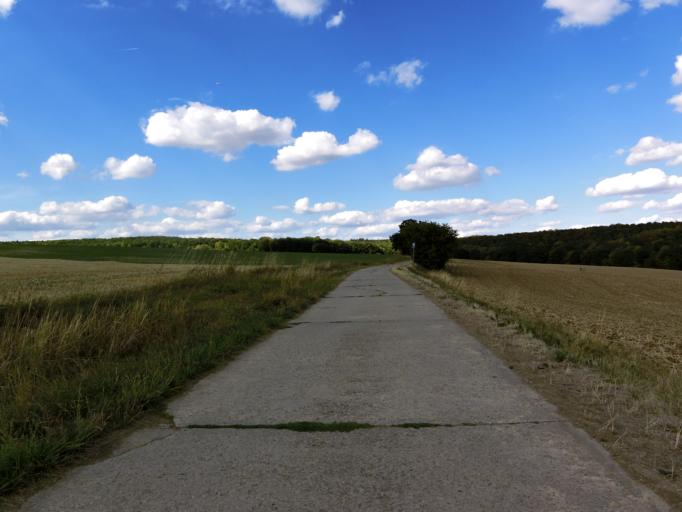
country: DE
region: Bavaria
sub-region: Regierungsbezirk Unterfranken
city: Veitshochheim
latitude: 49.8453
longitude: 9.8833
